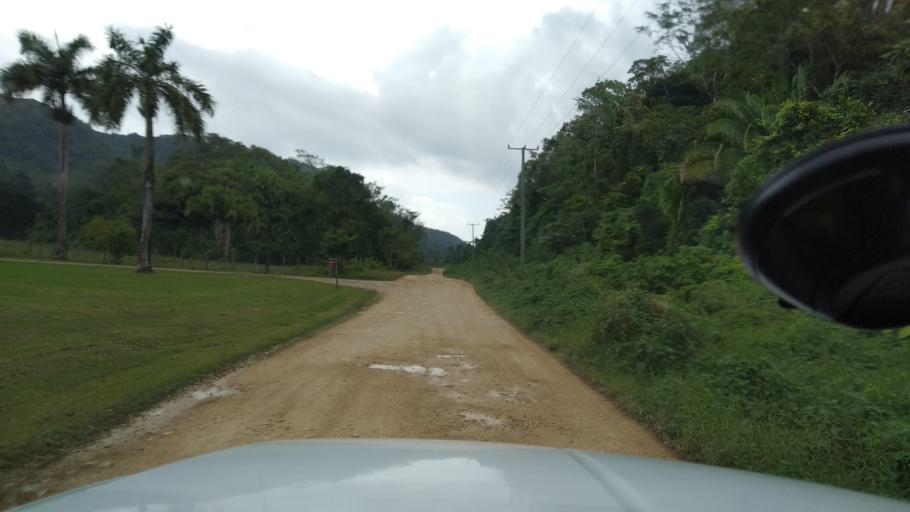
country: BZ
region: Toledo
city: Punta Gorda
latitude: 16.2066
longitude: -89.0283
